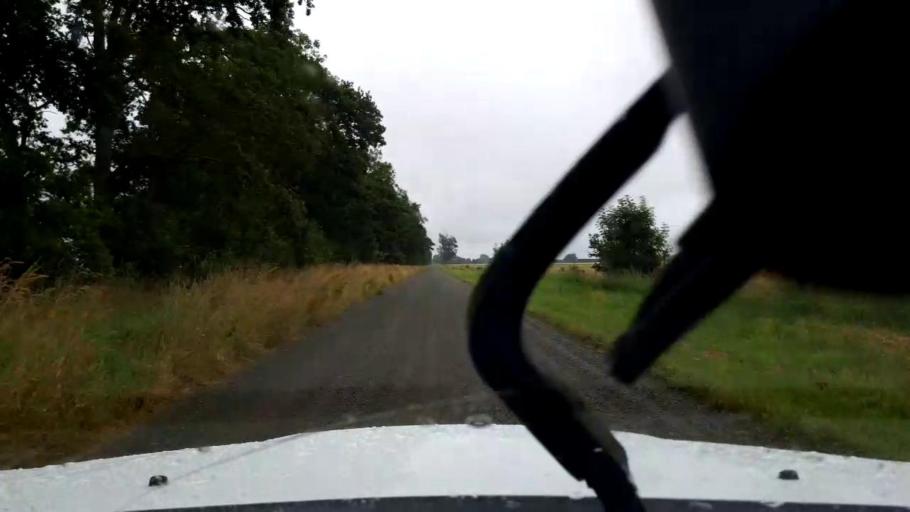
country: NZ
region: Canterbury
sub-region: Timaru District
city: Pleasant Point
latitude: -44.2096
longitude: 171.2814
